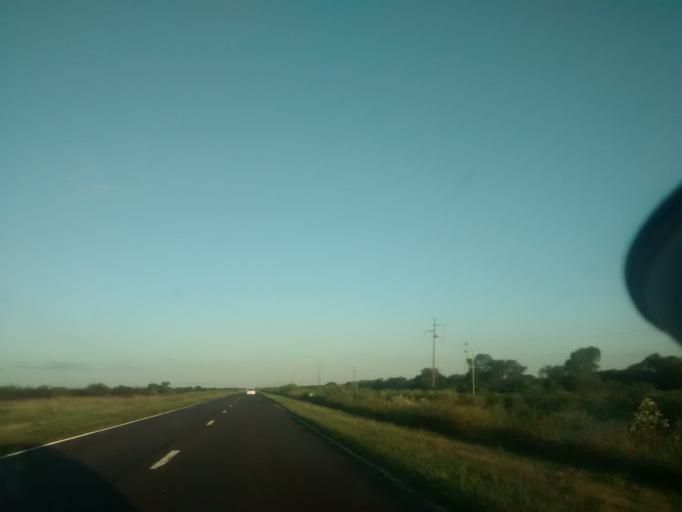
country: AR
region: Chaco
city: La Escondida
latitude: -27.0922
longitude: -59.6297
